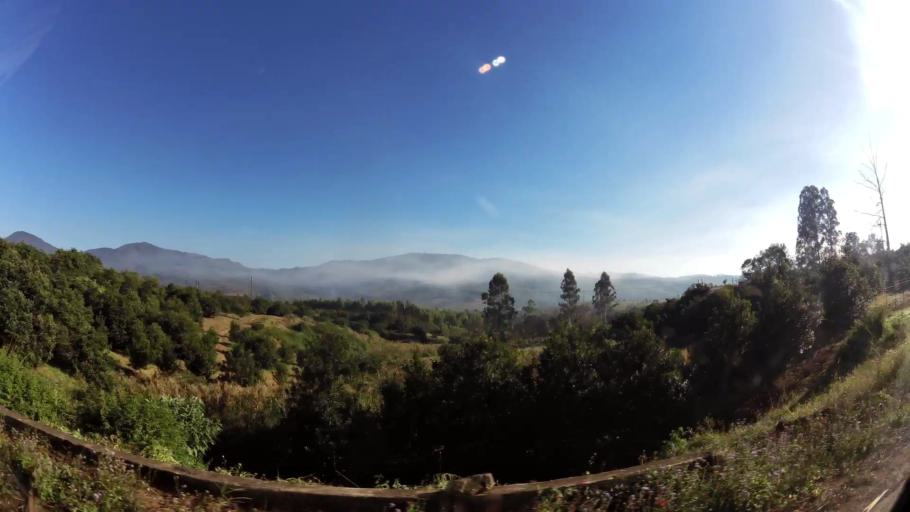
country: ZA
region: Limpopo
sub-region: Mopani District Municipality
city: Tzaneen
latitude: -23.8917
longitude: 30.0811
